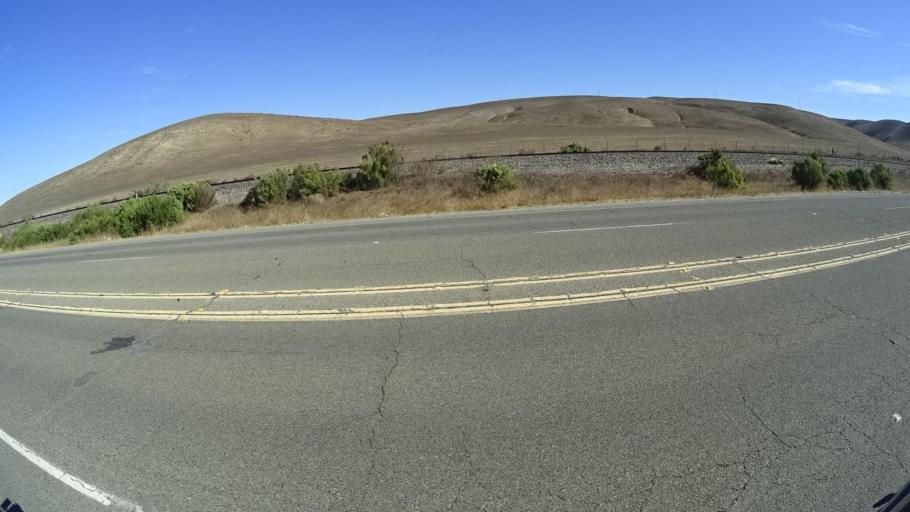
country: US
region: California
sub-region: Monterey County
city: King City
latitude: 36.1052
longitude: -120.9899
